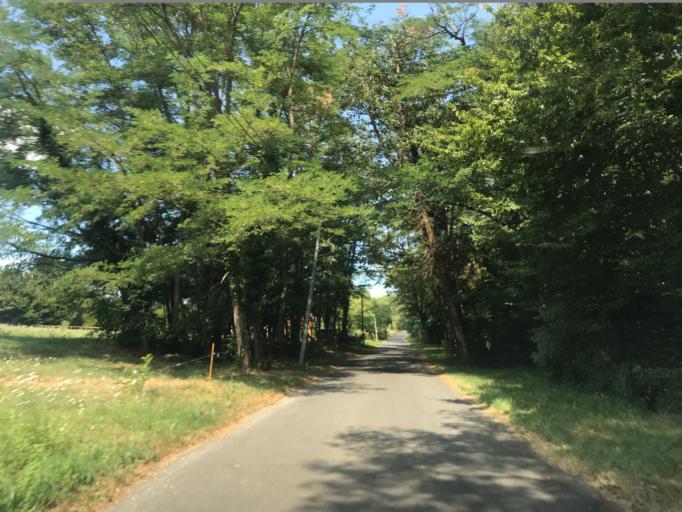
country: FR
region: Aquitaine
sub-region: Departement de la Dordogne
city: Cenac-et-Saint-Julien
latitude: 44.8316
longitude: 1.1914
